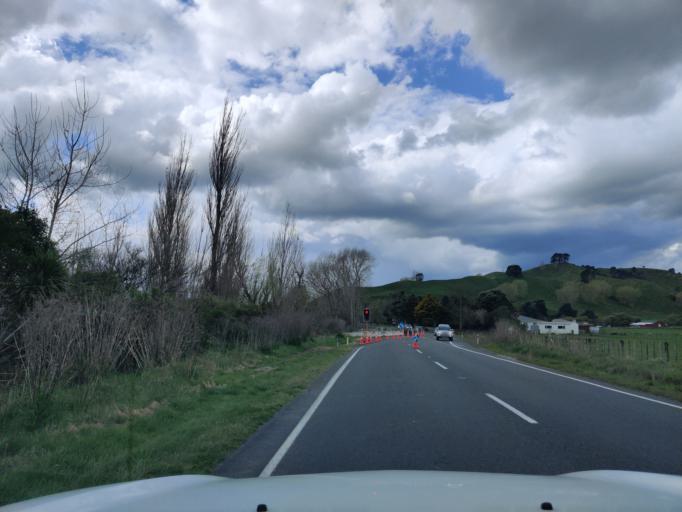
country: NZ
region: Manawatu-Wanganui
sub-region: Wanganui District
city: Wanganui
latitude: -39.8766
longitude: 175.1099
